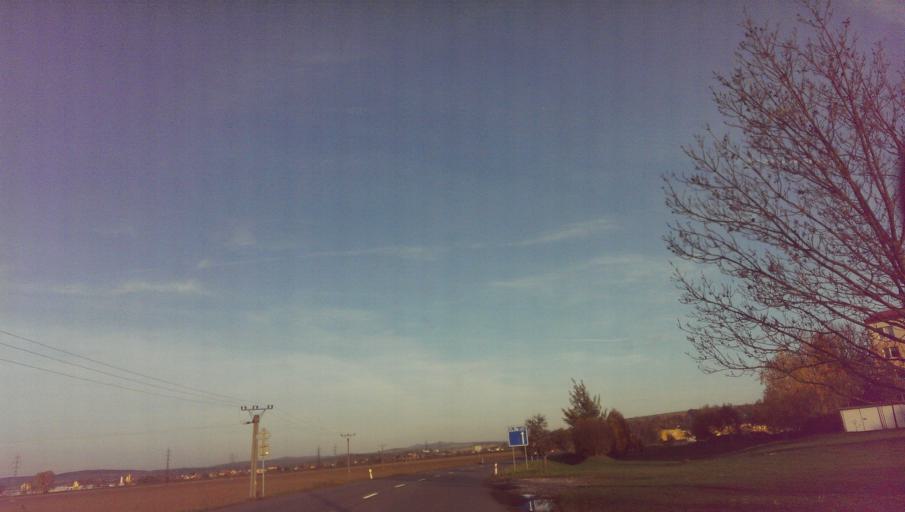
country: CZ
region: Zlin
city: Knezpole
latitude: 49.0898
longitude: 17.5003
